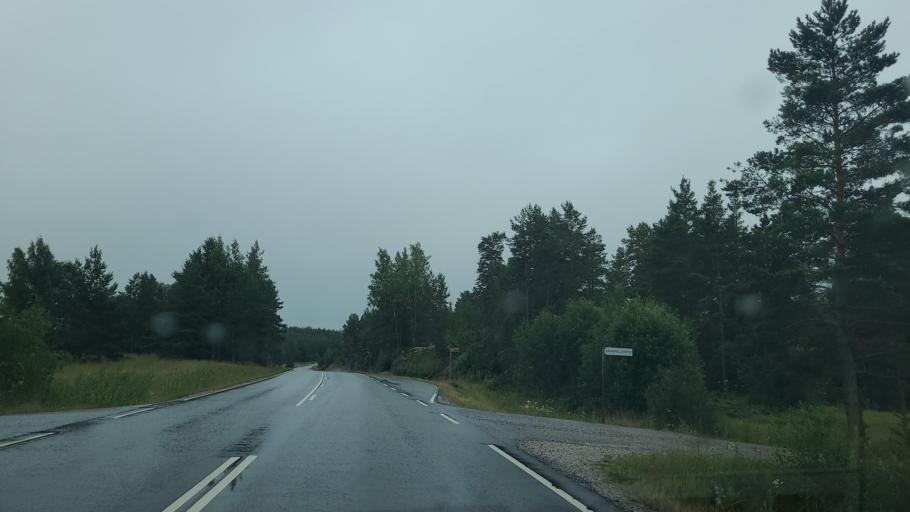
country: FI
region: Varsinais-Suomi
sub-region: Turku
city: Sauvo
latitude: 60.2779
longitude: 22.6684
